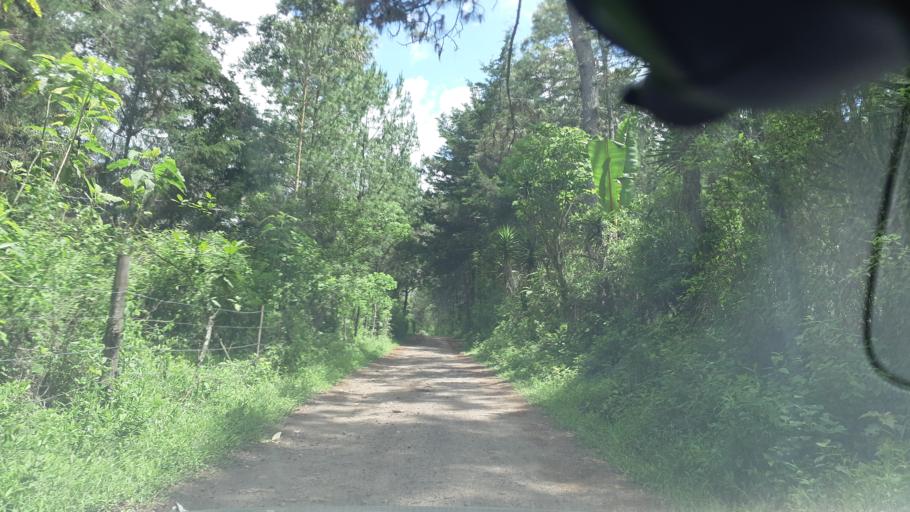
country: GT
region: Chimaltenango
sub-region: Municipio de Chimaltenango
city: Chimaltenango
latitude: 14.6584
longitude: -90.8479
